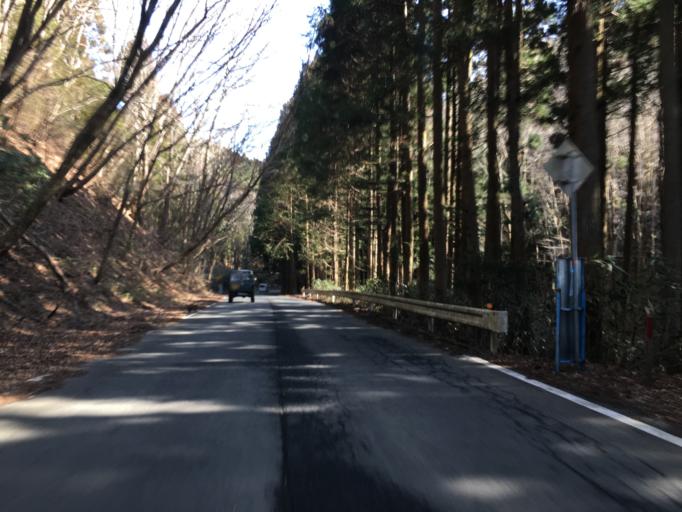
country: JP
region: Ibaraki
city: Kitaibaraki
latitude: 36.8318
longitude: 140.5655
